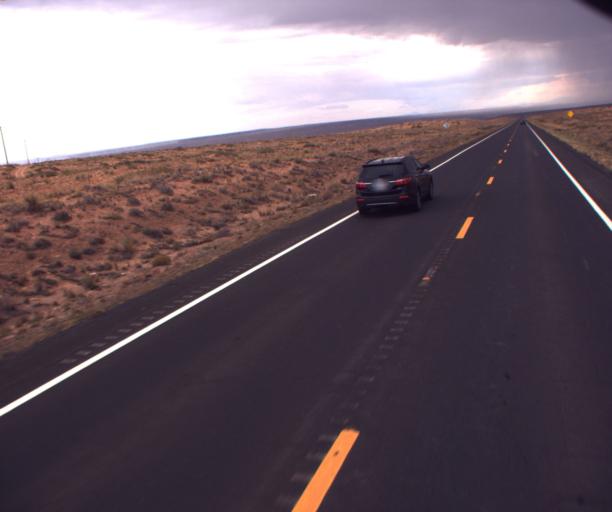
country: US
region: Arizona
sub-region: Coconino County
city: Tuba City
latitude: 36.2318
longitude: -111.0309
